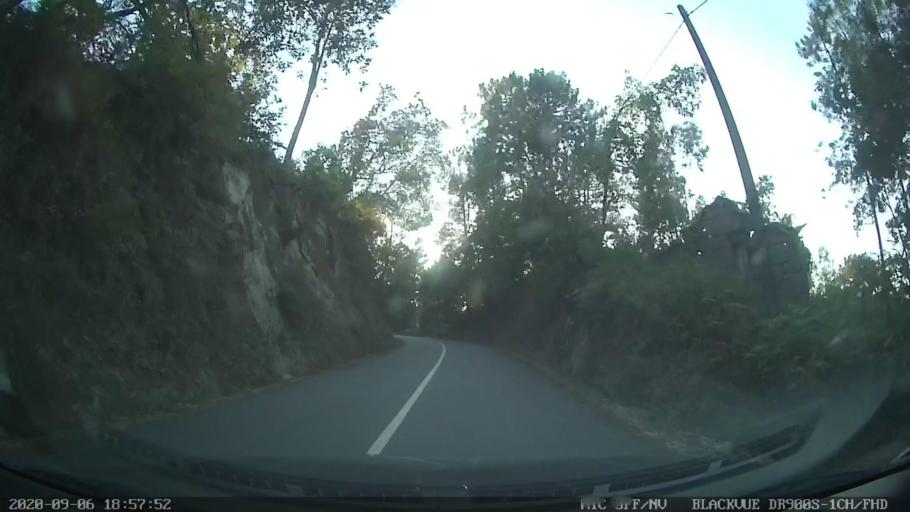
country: PT
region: Porto
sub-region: Baiao
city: Baiao
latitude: 41.2440
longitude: -7.9875
